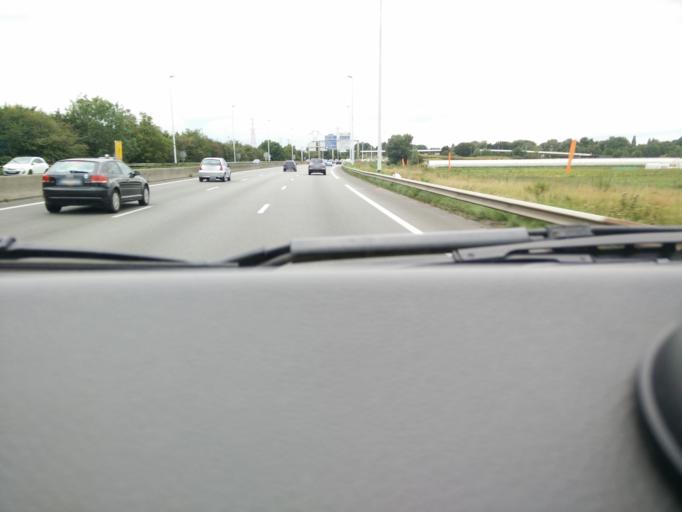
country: FR
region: Nord-Pas-de-Calais
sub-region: Departement du Nord
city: Wasquehal
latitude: 50.6498
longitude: 3.1393
